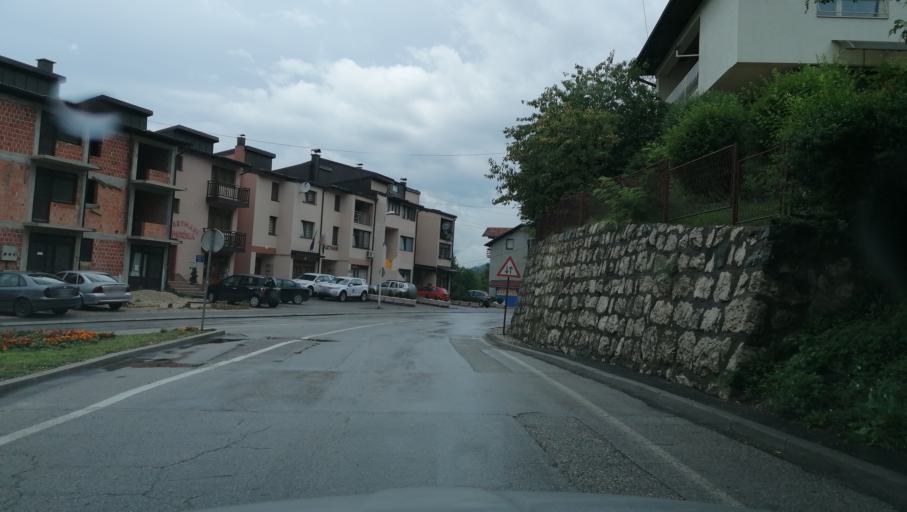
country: BA
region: Republika Srpska
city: Visegrad
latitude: 43.7860
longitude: 19.2963
